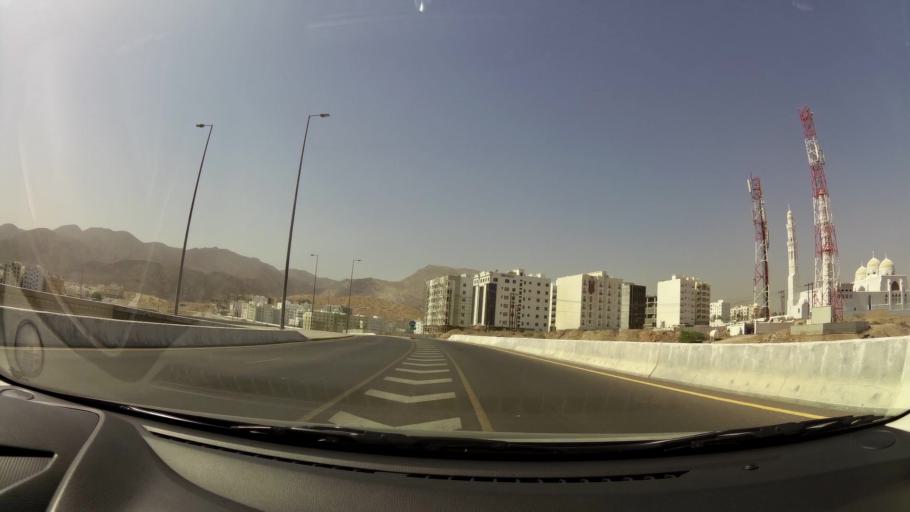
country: OM
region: Muhafazat Masqat
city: Bawshar
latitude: 23.5808
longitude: 58.4164
